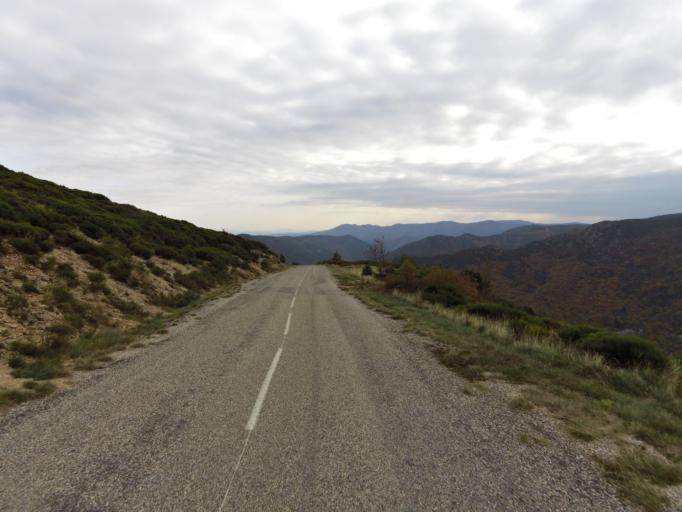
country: FR
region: Rhone-Alpes
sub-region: Departement de l'Ardeche
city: Les Vans
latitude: 44.5042
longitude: 4.0446
